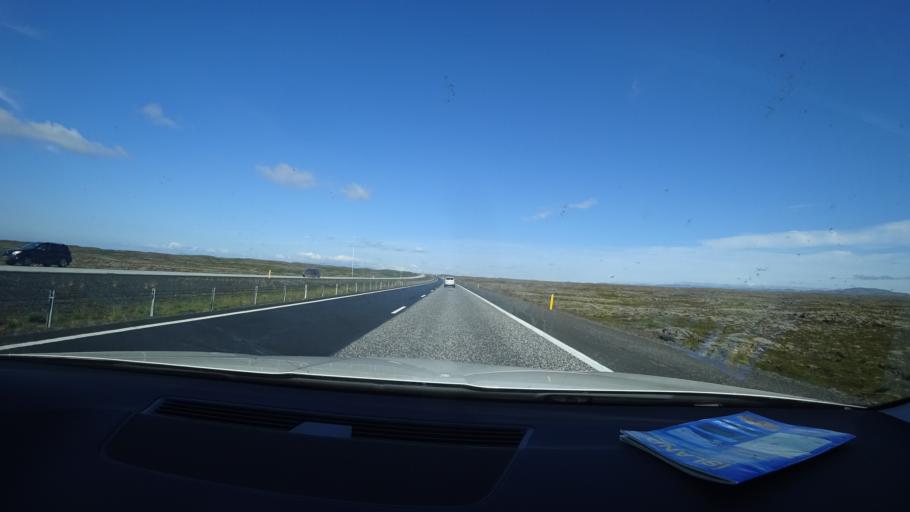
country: IS
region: Southern Peninsula
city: Vogar
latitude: 63.9886
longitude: -22.2989
